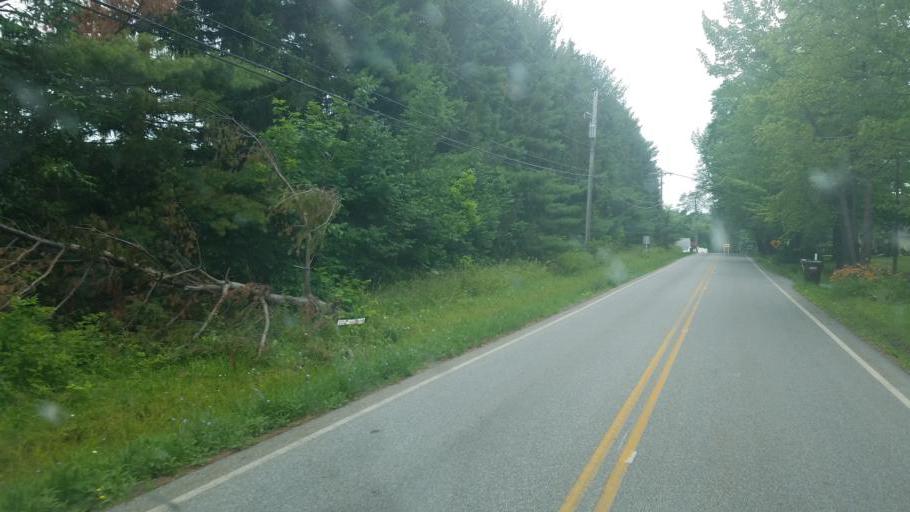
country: US
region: Ohio
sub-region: Geauga County
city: Burton
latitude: 41.4810
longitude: -81.1956
